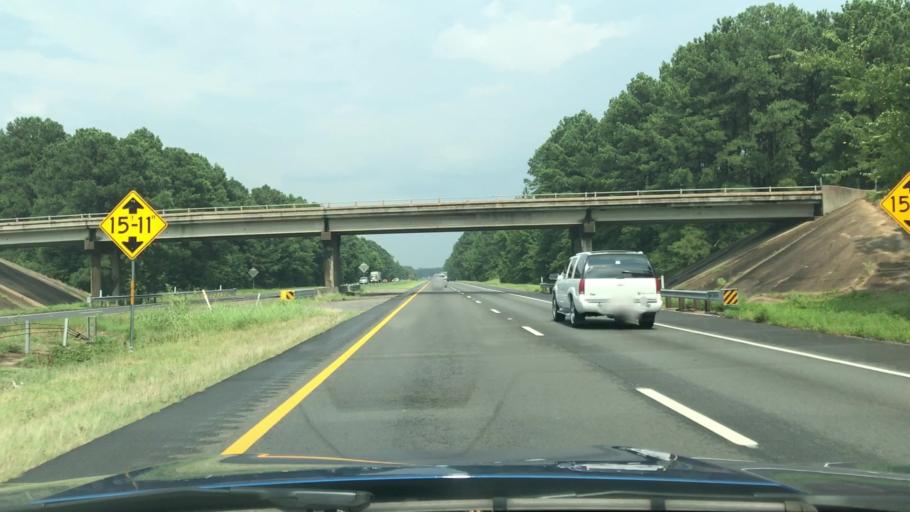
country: US
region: Texas
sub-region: Harrison County
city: Hallsville
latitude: 32.4801
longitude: -94.5453
